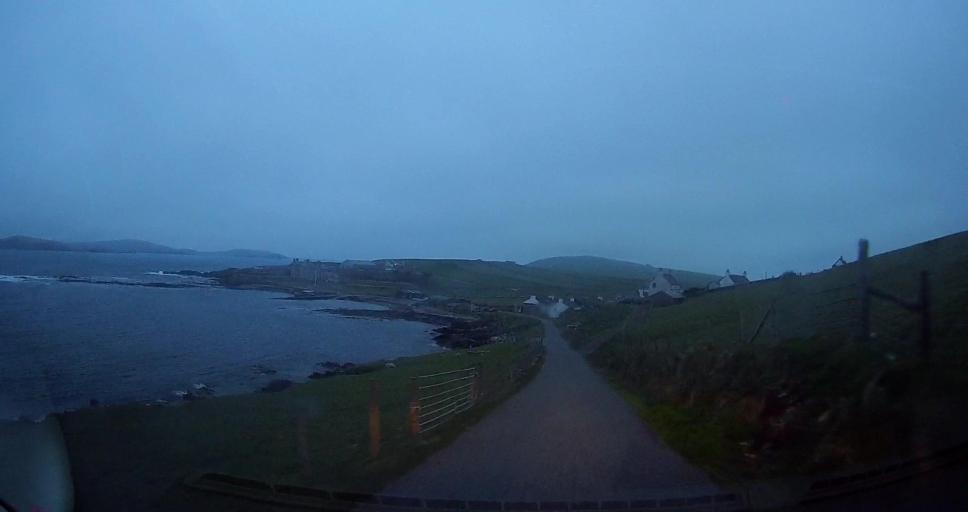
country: GB
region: Scotland
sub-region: Shetland Islands
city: Sandwick
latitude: 60.0088
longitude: -1.2250
